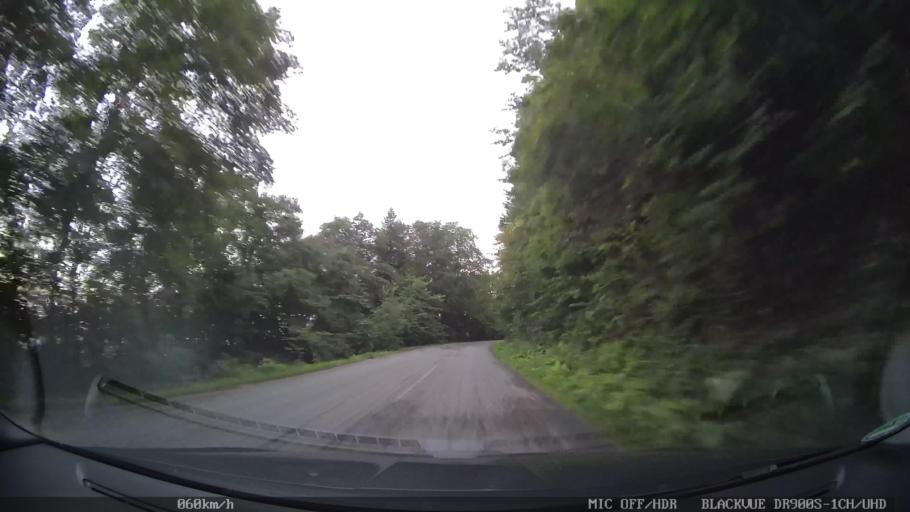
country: HR
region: Primorsko-Goranska
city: Vrbovsko
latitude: 45.1828
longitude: 14.9892
